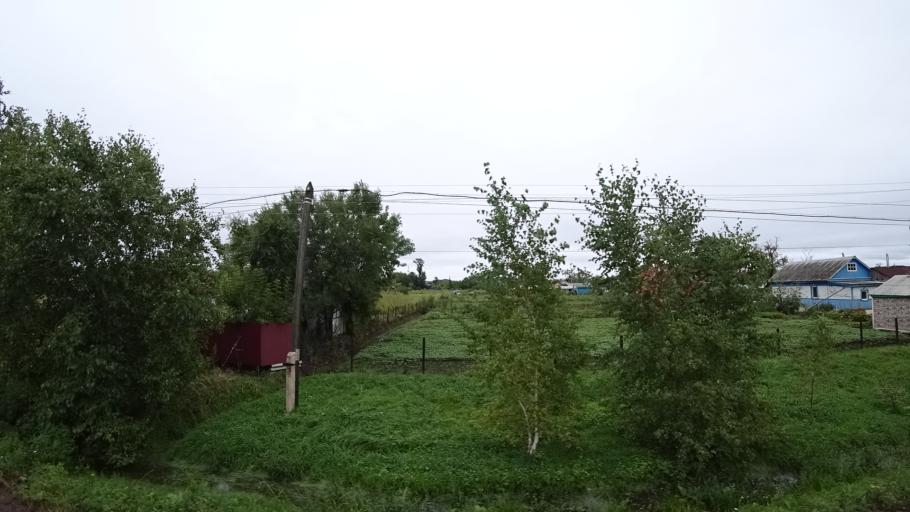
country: RU
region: Primorskiy
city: Monastyrishche
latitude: 44.2024
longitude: 132.4684
